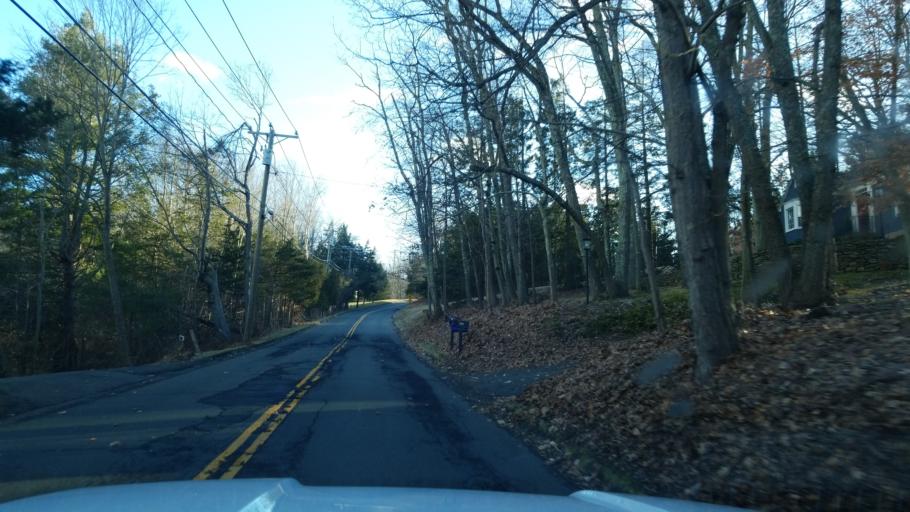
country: US
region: Connecticut
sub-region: Middlesex County
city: Durham
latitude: 41.5132
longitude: -72.6484
